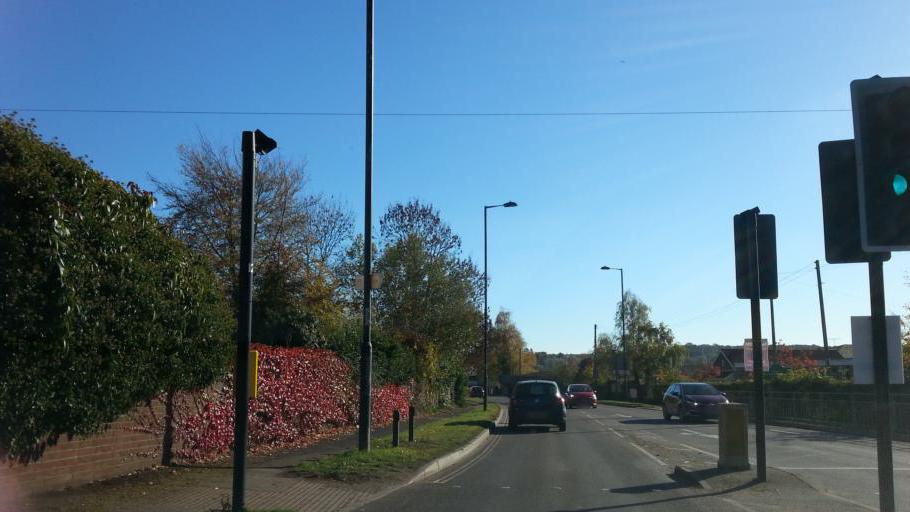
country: GB
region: England
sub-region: Suffolk
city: Woodbridge
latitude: 52.1050
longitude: 1.3300
